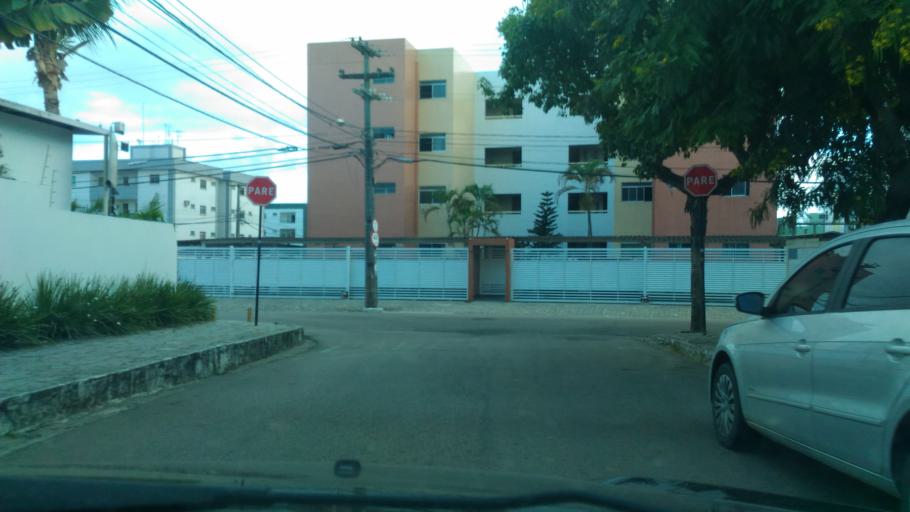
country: BR
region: Paraiba
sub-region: Joao Pessoa
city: Joao Pessoa
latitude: -7.1531
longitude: -34.8363
